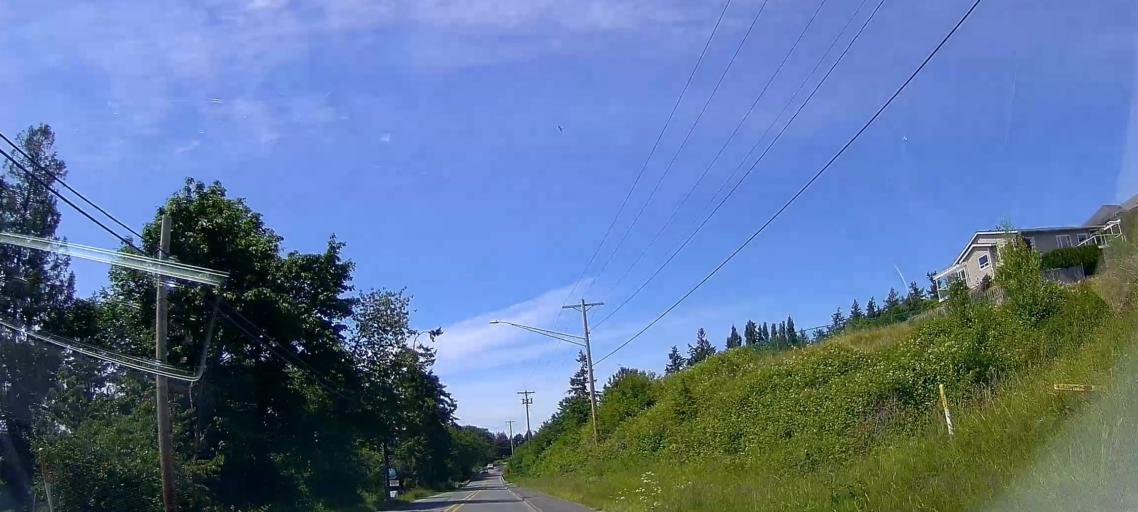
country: US
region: Washington
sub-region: Snohomish County
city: Stanwood
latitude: 48.2517
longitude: -122.3528
